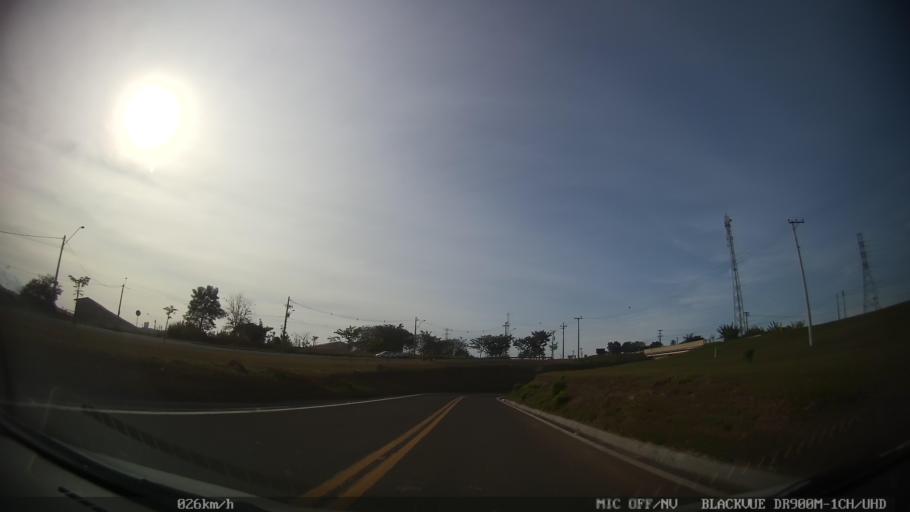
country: BR
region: Sao Paulo
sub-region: Piracicaba
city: Piracicaba
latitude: -22.6780
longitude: -47.7146
